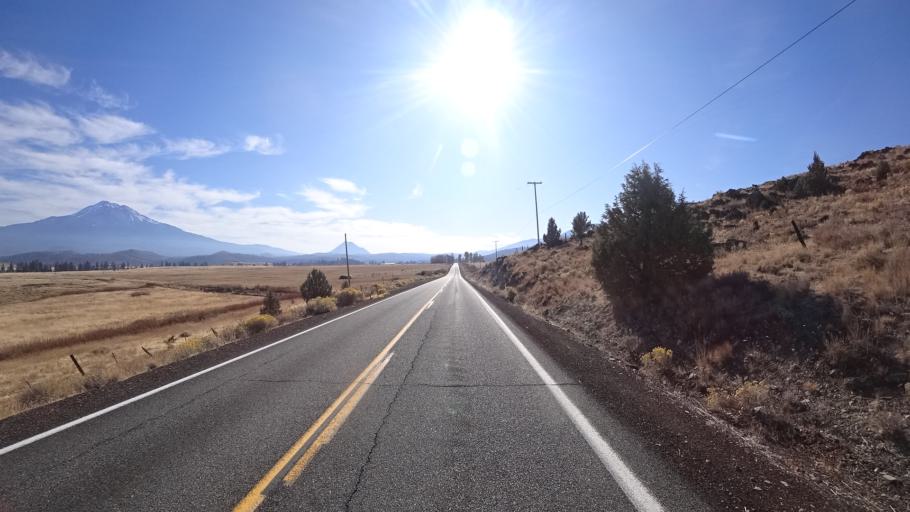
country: US
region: California
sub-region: Siskiyou County
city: Weed
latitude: 41.4659
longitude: -122.4662
